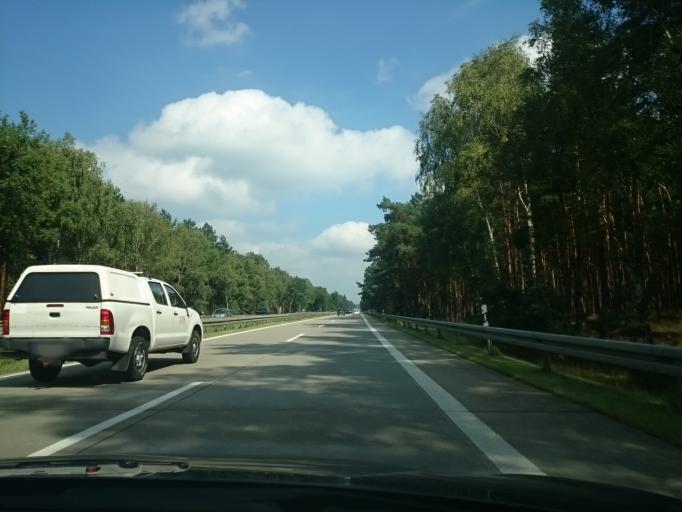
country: DE
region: Brandenburg
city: Marienwerder
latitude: 52.7963
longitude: 13.6007
